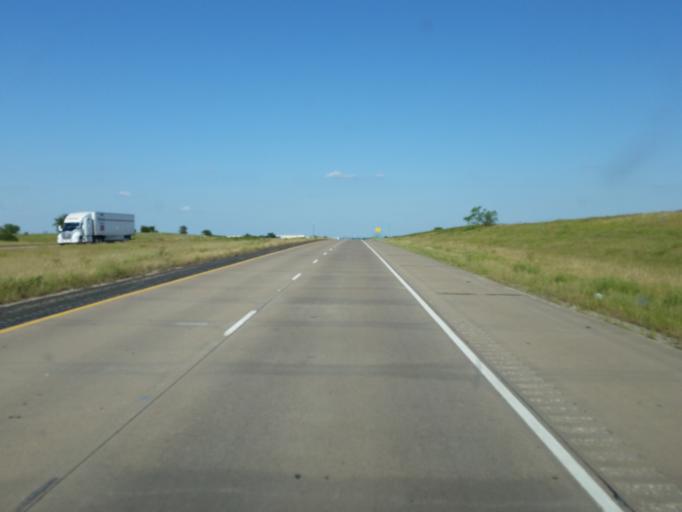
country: US
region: Texas
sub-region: Tarrant County
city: Benbrook
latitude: 32.6954
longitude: -97.5292
